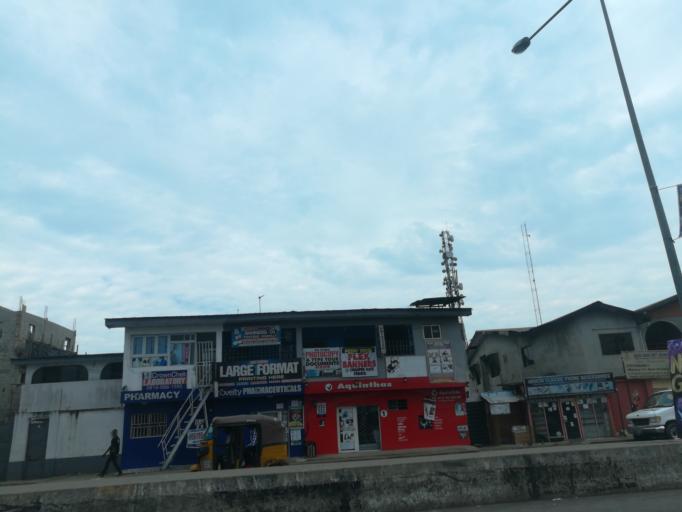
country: NG
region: Rivers
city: Port Harcourt
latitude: 4.8520
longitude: 6.9752
